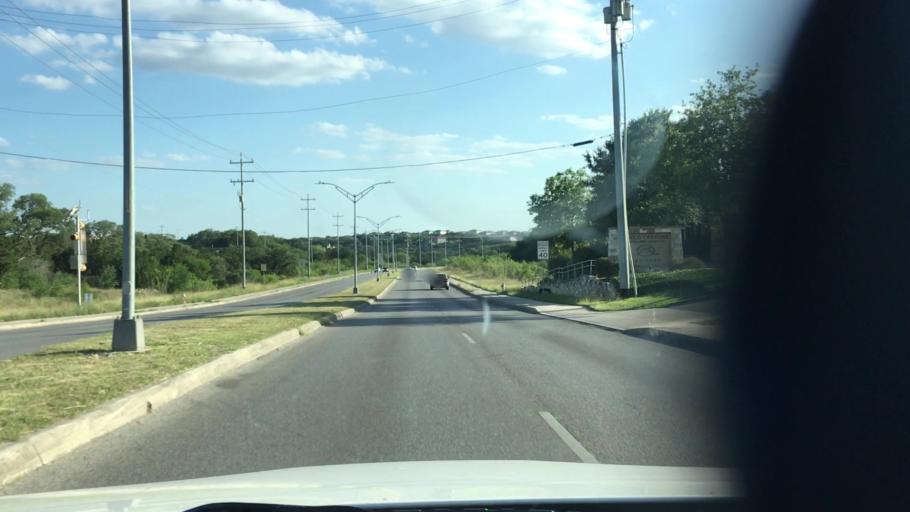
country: US
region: Texas
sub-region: Bexar County
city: Timberwood Park
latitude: 29.6574
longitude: -98.4391
